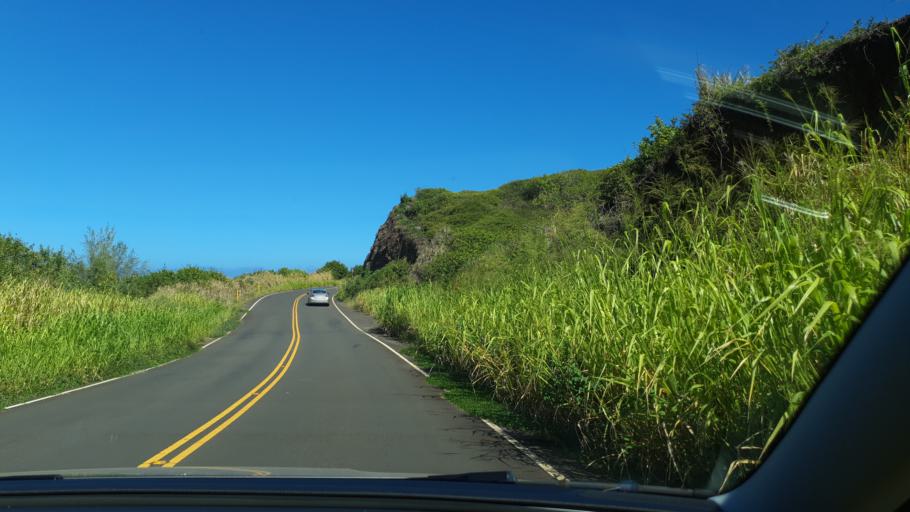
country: US
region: Hawaii
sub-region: Maui County
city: Napili-Honokowai
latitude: 21.0122
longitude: -156.5711
